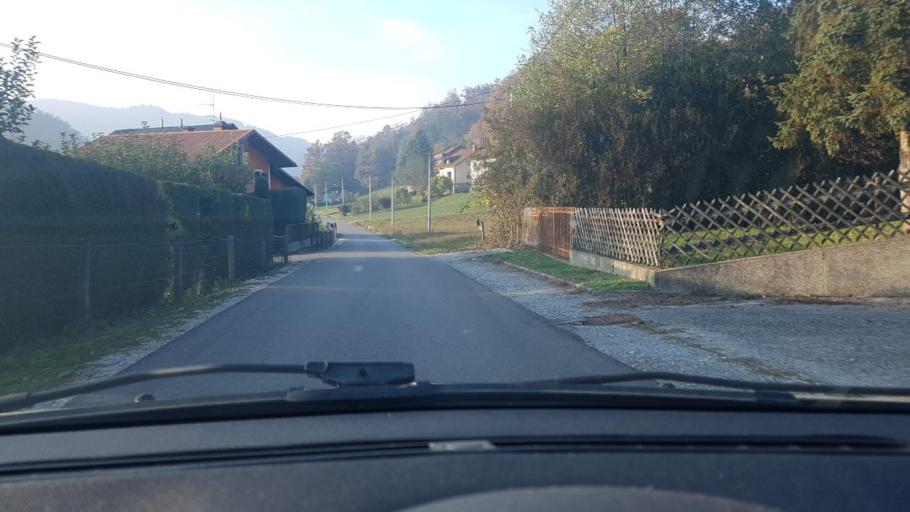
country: SI
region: Podcetrtek
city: Podcetrtek
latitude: 46.1569
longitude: 15.6138
